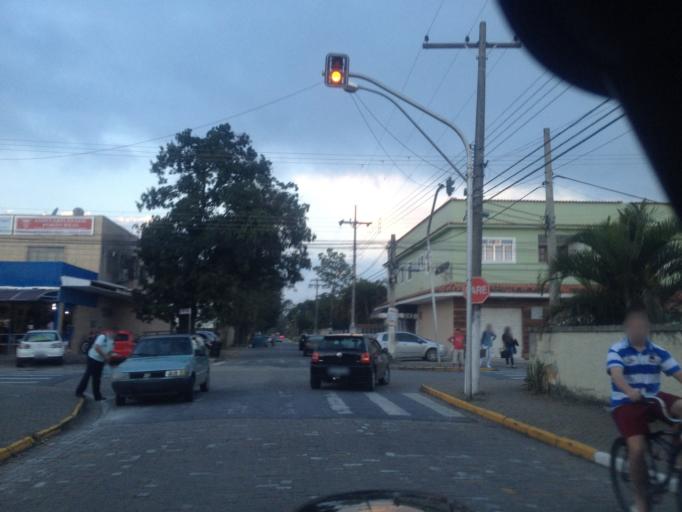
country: BR
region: Rio de Janeiro
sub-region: Porto Real
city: Porto Real
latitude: -22.4166
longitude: -44.2935
